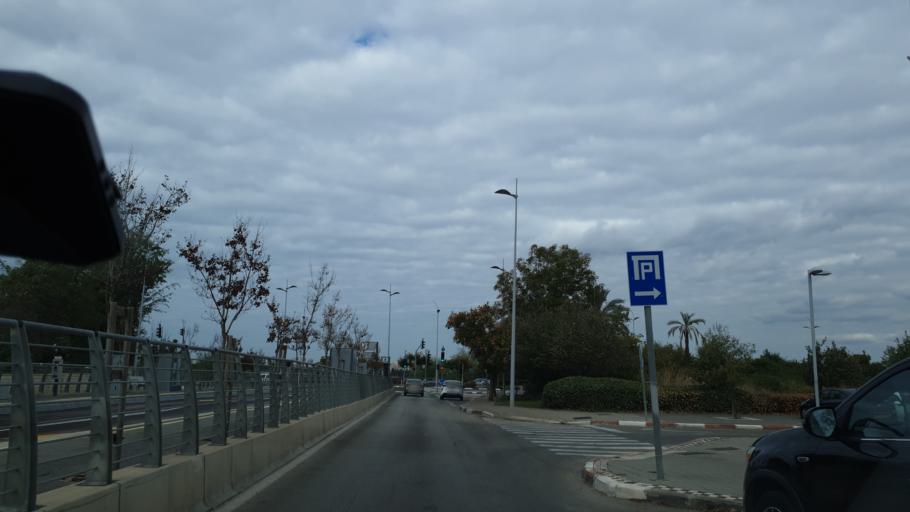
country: IL
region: Haifa
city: Qiryat Ata
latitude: 32.8176
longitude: 35.1132
